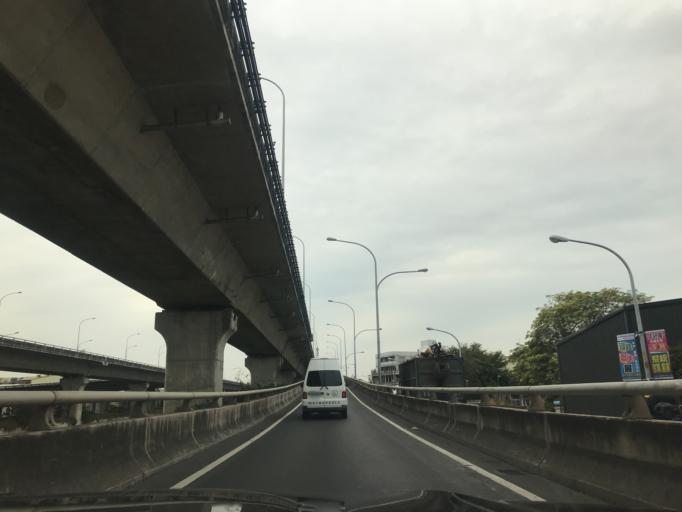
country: TW
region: Taiwan
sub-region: Nantou
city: Nantou
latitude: 23.9474
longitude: 120.5601
